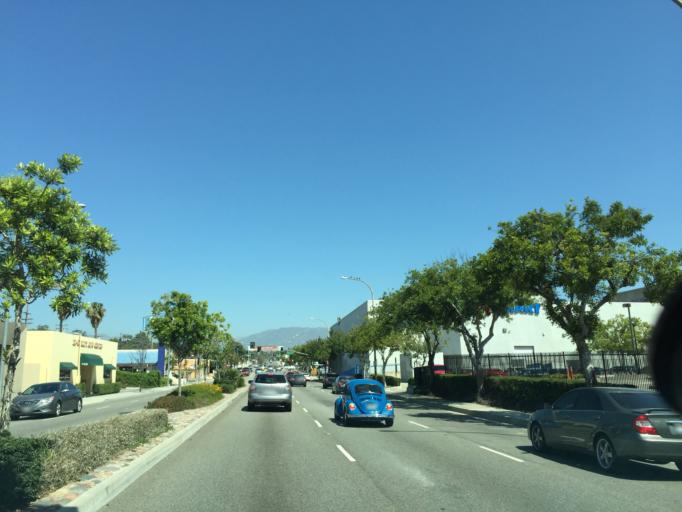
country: US
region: California
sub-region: Los Angeles County
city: Alhambra
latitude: 34.0853
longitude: -118.1519
